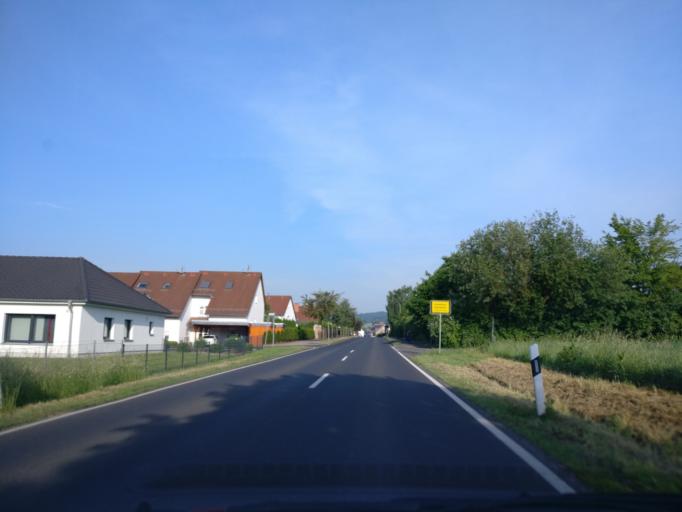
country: DE
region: Hesse
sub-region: Regierungsbezirk Kassel
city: Baunatal
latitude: 51.2726
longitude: 9.3871
